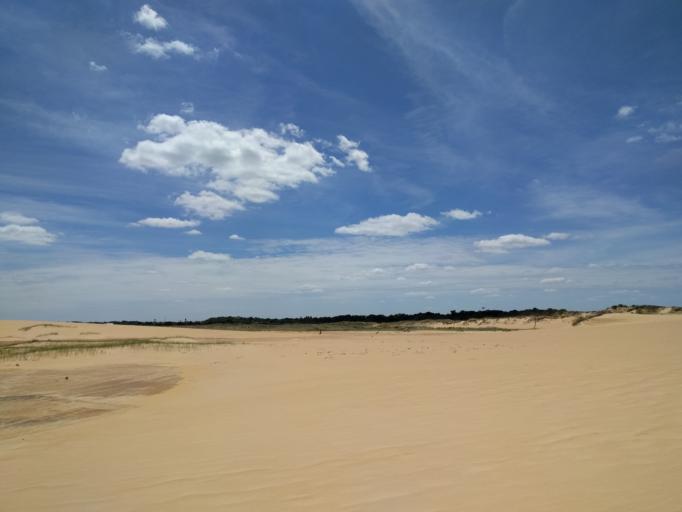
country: BO
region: Santa Cruz
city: Santa Cruz de la Sierra
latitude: -17.9446
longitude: -63.1529
